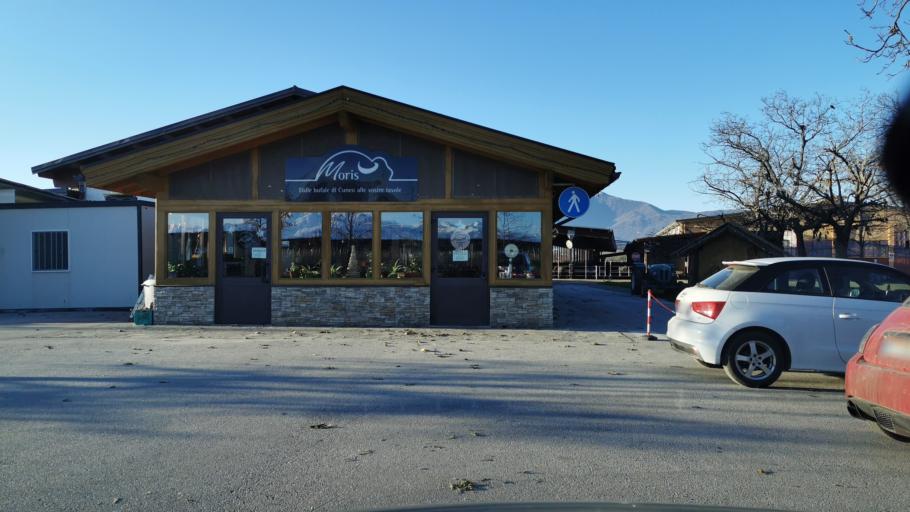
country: IT
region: Piedmont
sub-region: Provincia di Cuneo
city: Caraglio
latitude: 44.4358
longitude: 7.4453
